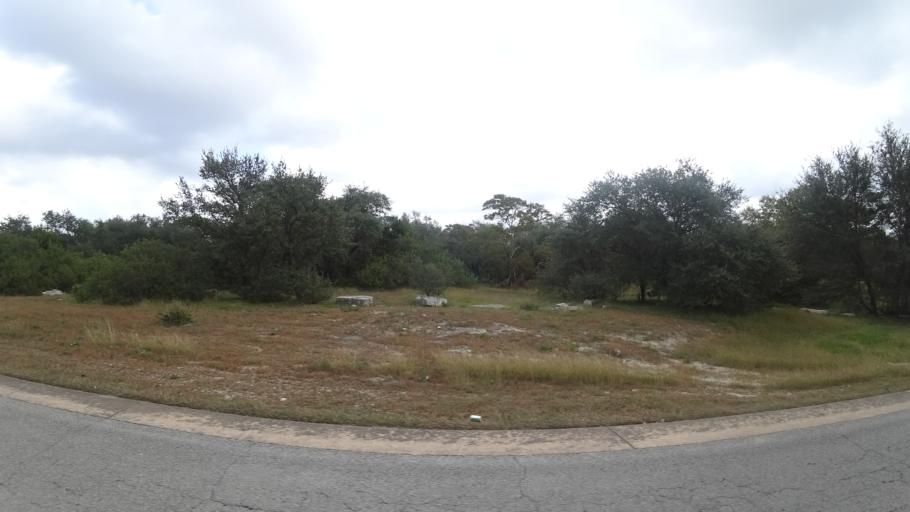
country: US
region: Texas
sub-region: Travis County
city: Barton Creek
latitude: 30.3060
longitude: -97.8924
